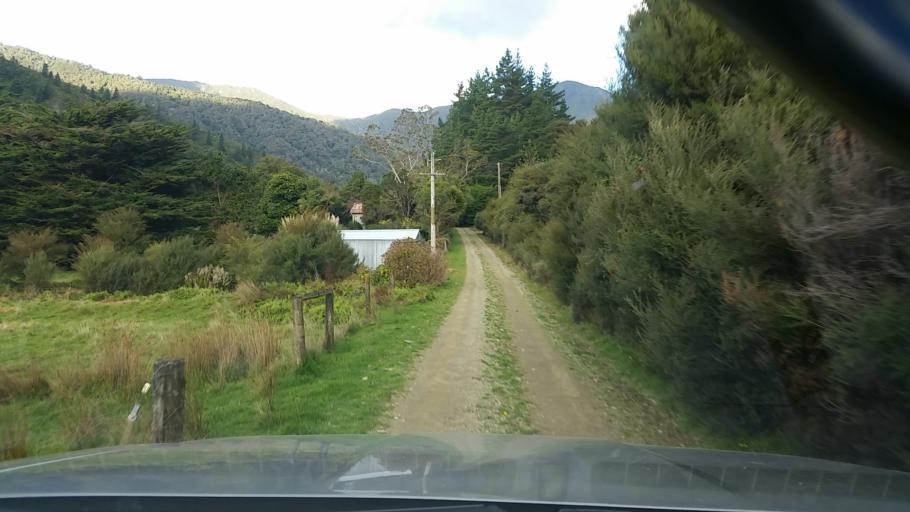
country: NZ
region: Marlborough
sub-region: Marlborough District
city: Picton
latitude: -41.0586
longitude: 174.1113
